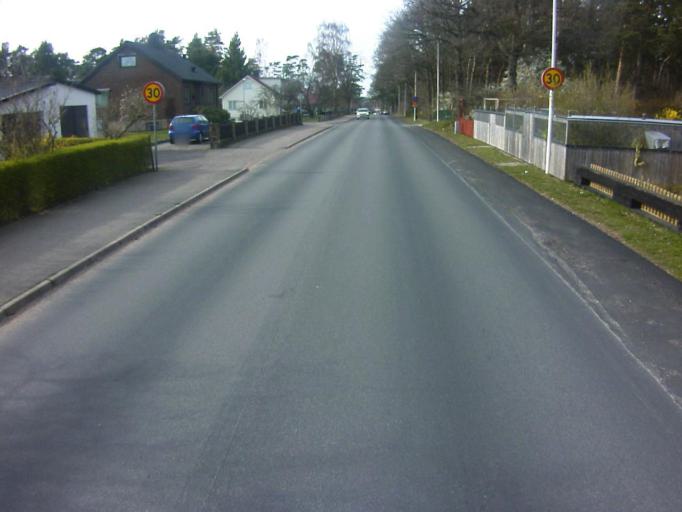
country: SE
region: Skane
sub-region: Kavlinge Kommun
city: Kaevlinge
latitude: 55.7738
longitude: 13.0878
